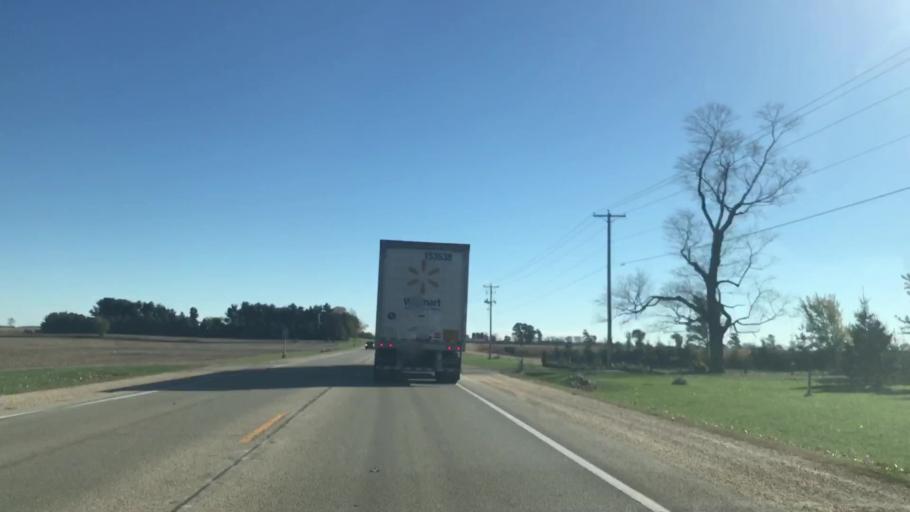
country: US
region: Wisconsin
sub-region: Dodge County
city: Juneau
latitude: 43.4446
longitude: -88.6930
